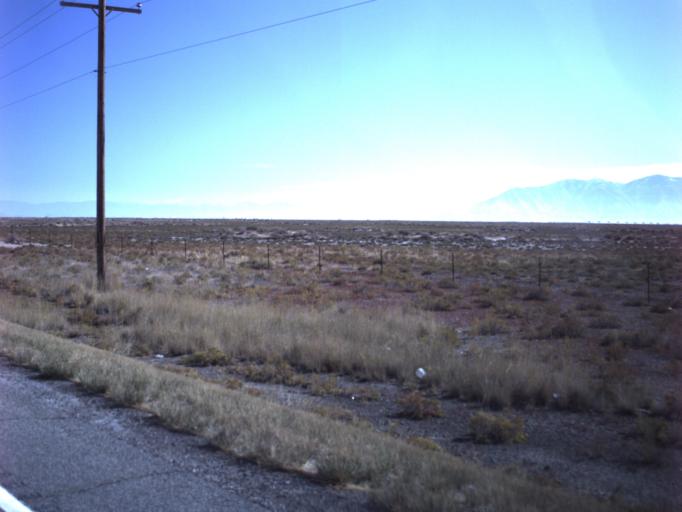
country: US
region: Utah
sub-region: Tooele County
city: Grantsville
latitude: 40.6949
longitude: -112.5321
